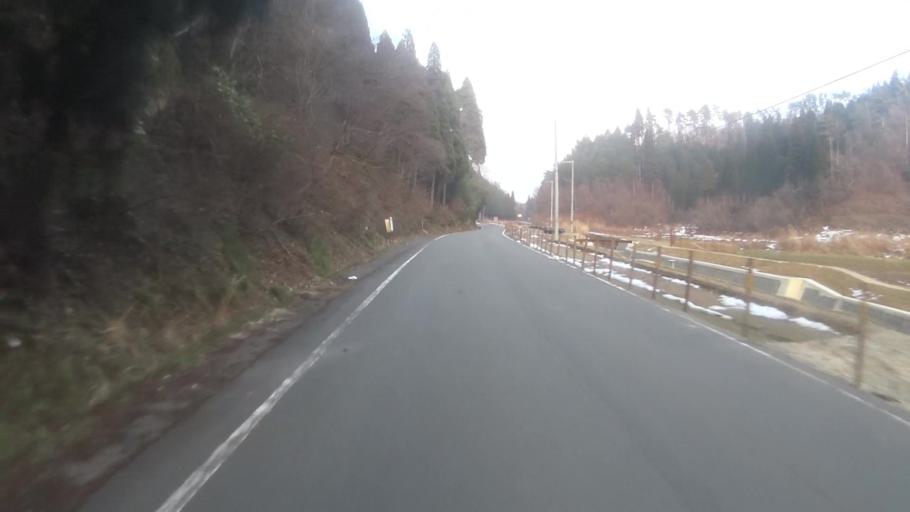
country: JP
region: Kyoto
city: Maizuru
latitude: 35.4370
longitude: 135.4843
